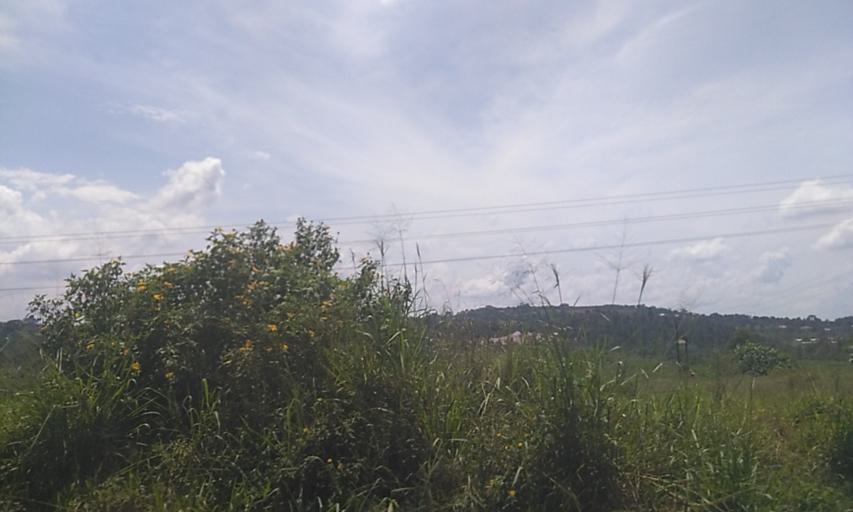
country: UG
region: Central Region
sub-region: Wakiso District
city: Wakiso
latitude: 0.4133
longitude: 32.4535
